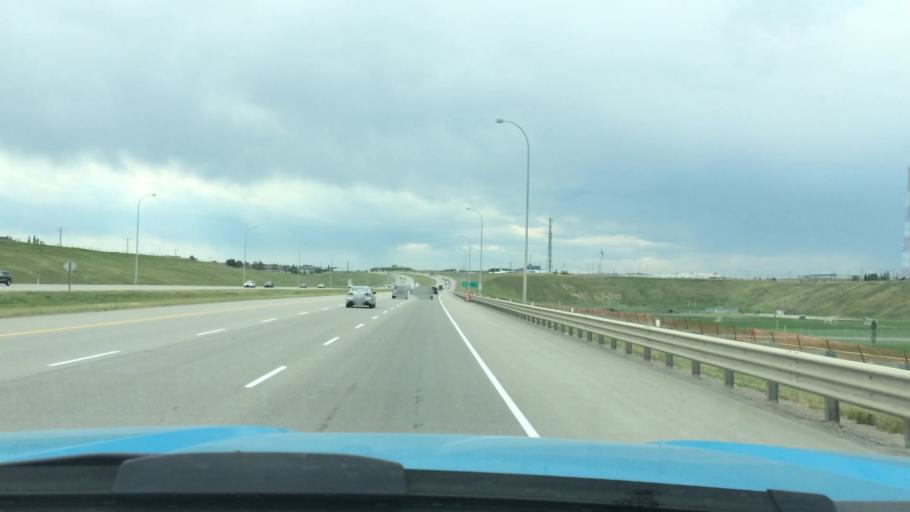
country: CA
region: Alberta
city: Calgary
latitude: 51.1515
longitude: -114.1756
